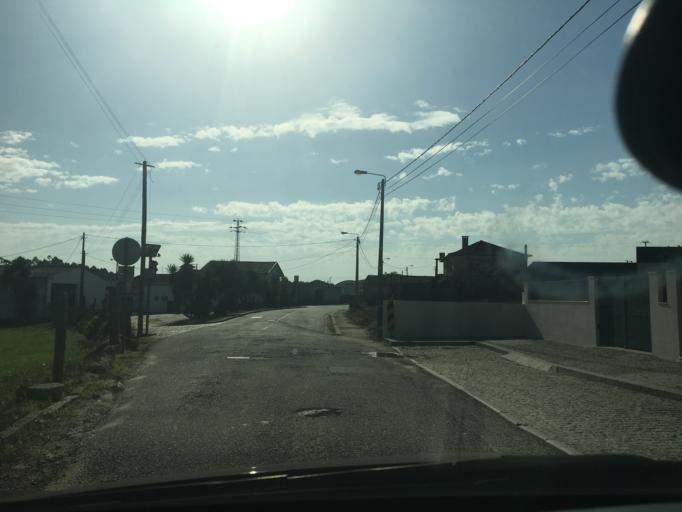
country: PT
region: Porto
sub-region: Maia
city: Gemunde
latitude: 41.2504
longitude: -8.6417
